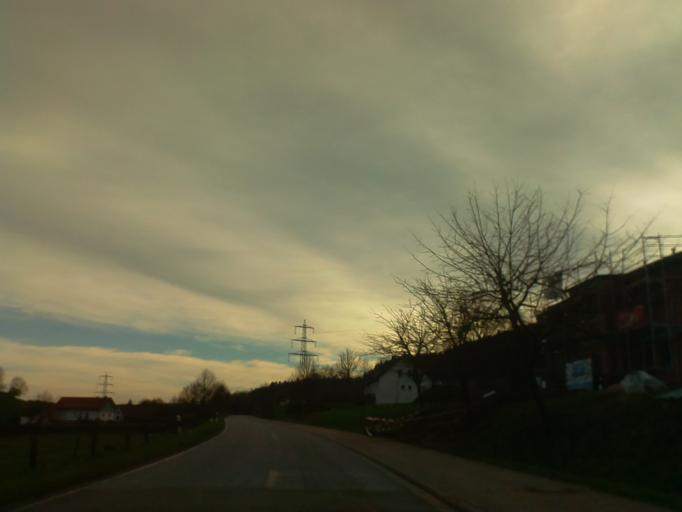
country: DE
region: Hesse
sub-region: Regierungsbezirk Darmstadt
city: Erbach
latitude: 49.6698
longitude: 8.9248
